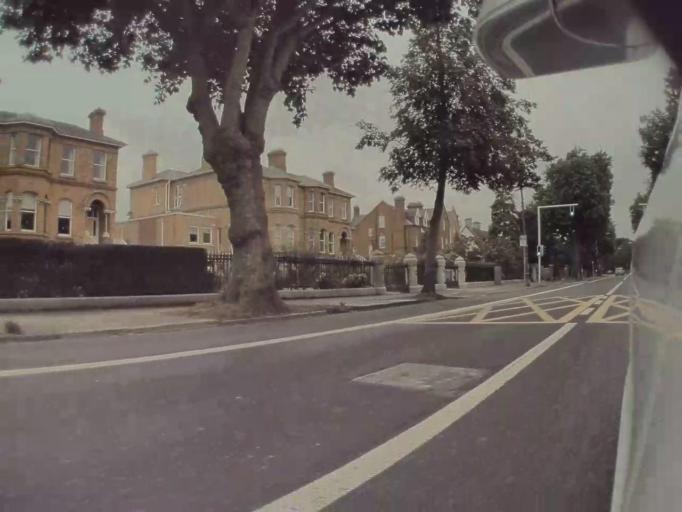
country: IE
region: Leinster
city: Donnybrook
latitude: 53.3223
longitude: -6.2180
